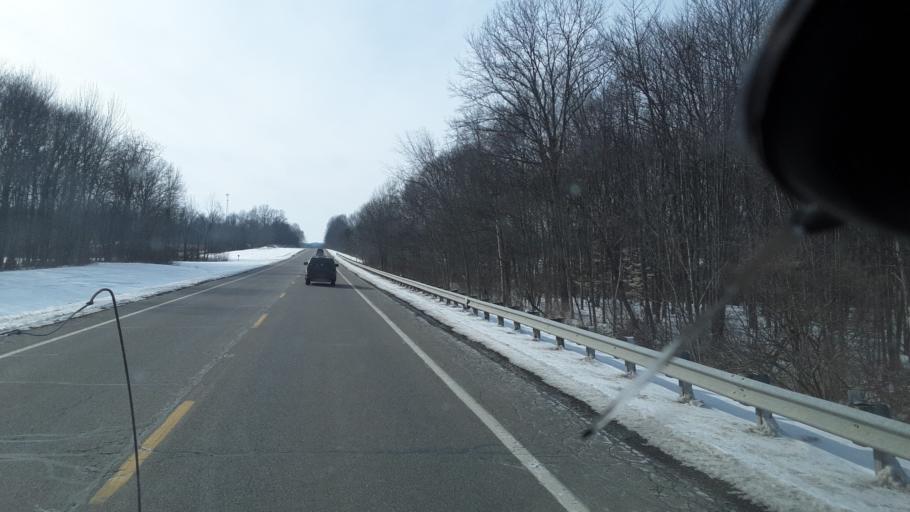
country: US
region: Ohio
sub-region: Stark County
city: Hartville
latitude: 41.0302
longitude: -81.2353
